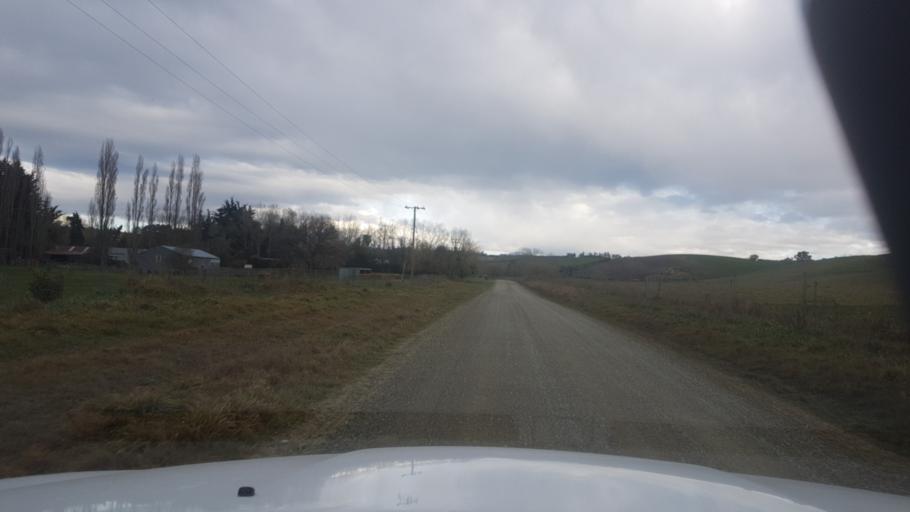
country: NZ
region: Canterbury
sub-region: Timaru District
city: Pleasant Point
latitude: -44.3395
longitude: 171.1730
